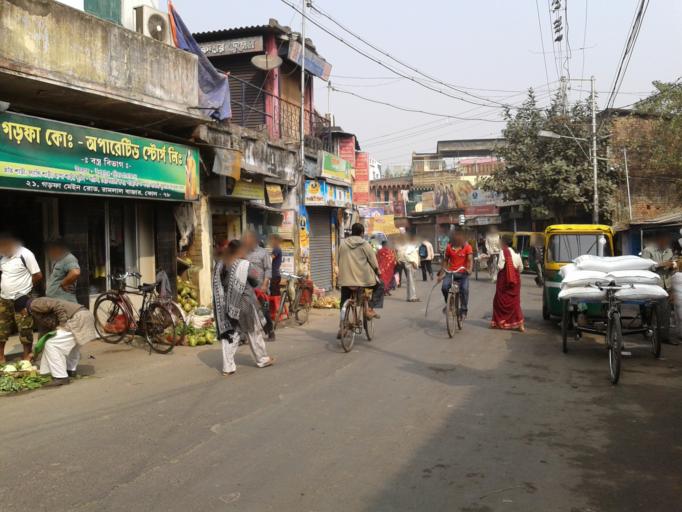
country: IN
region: West Bengal
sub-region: Kolkata
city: Kolkata
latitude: 22.5049
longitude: 88.3845
